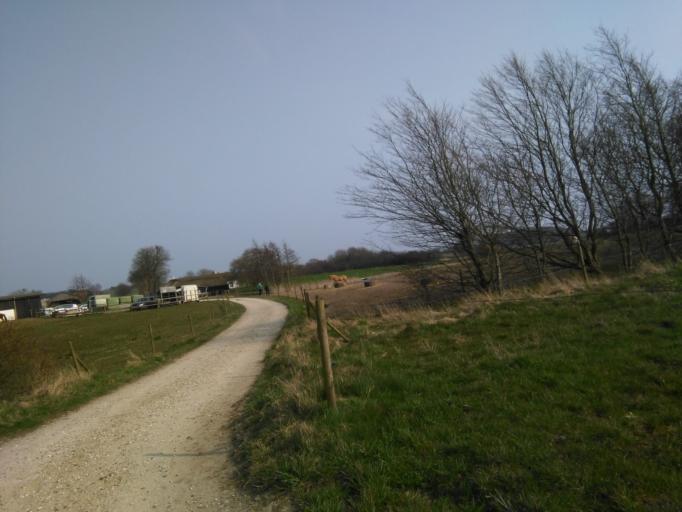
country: DK
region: Central Jutland
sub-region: Arhus Kommune
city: Beder
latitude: 56.0639
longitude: 10.2283
